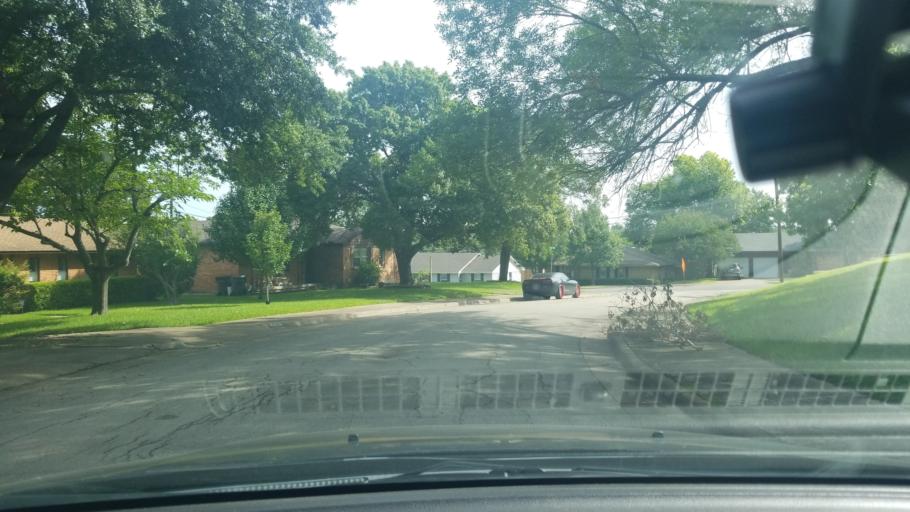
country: US
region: Texas
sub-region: Dallas County
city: Highland Park
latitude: 32.8101
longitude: -96.7027
